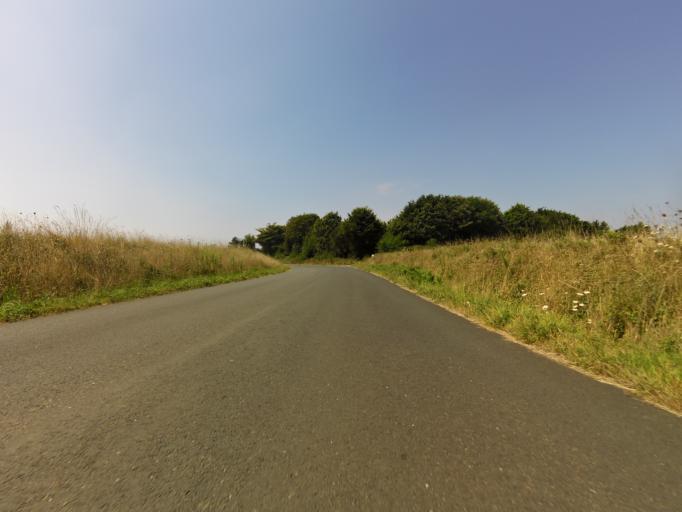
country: FR
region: Brittany
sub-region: Departement du Finistere
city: Pouldreuzic
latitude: 47.9072
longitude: -4.3501
